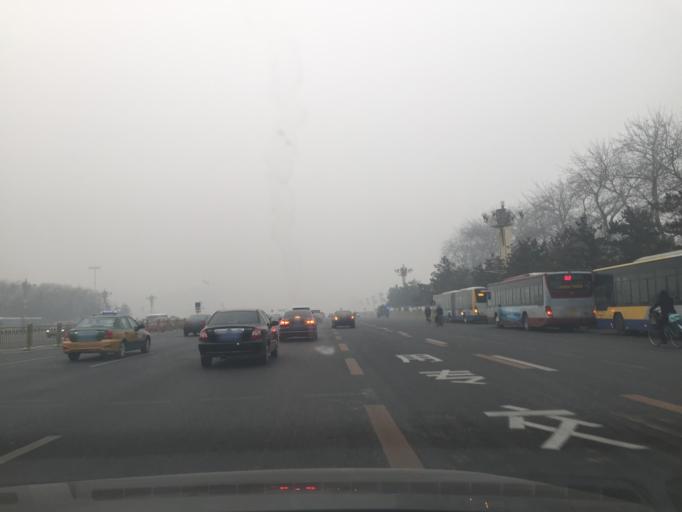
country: CN
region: Beijing
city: Beijing
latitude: 39.9065
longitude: 116.3962
